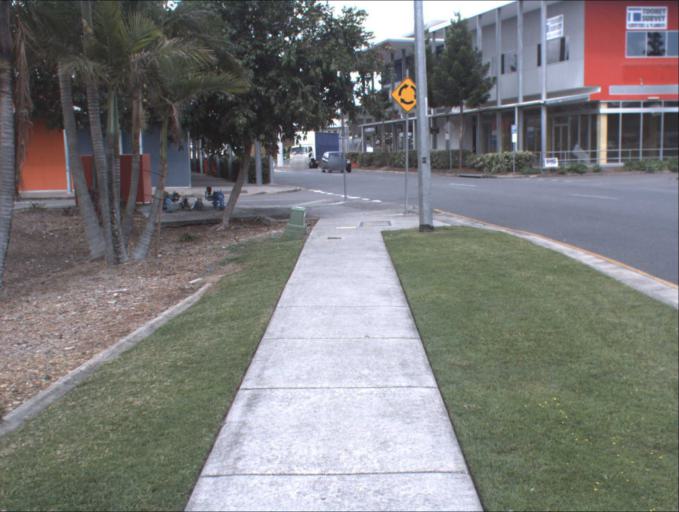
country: AU
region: Queensland
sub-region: Brisbane
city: Sunnybank Hills
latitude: -27.6630
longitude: 153.0458
